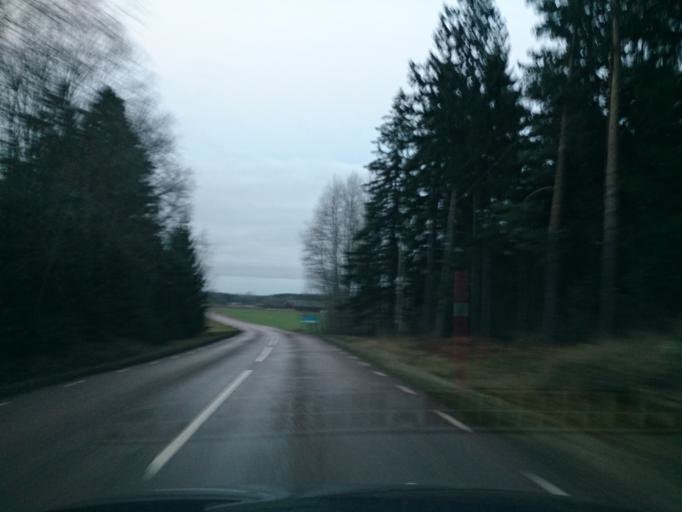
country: SE
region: OEstergoetland
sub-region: Linkopings Kommun
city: Linghem
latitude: 58.4584
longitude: 15.8847
